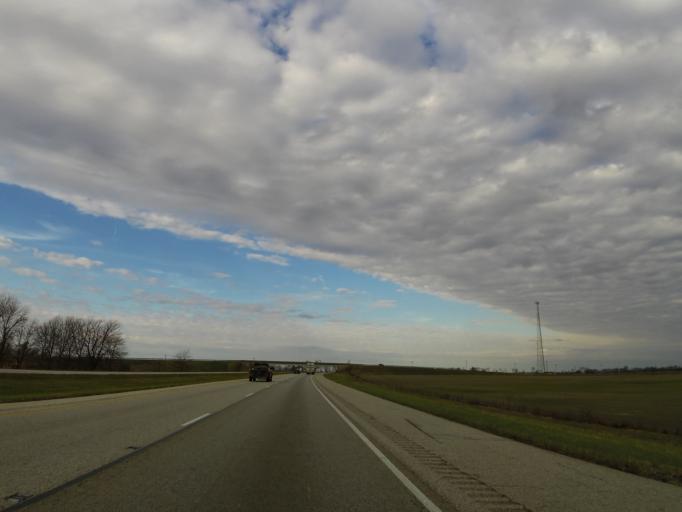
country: US
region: Illinois
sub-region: Washington County
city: Nashville
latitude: 38.4124
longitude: -89.4323
